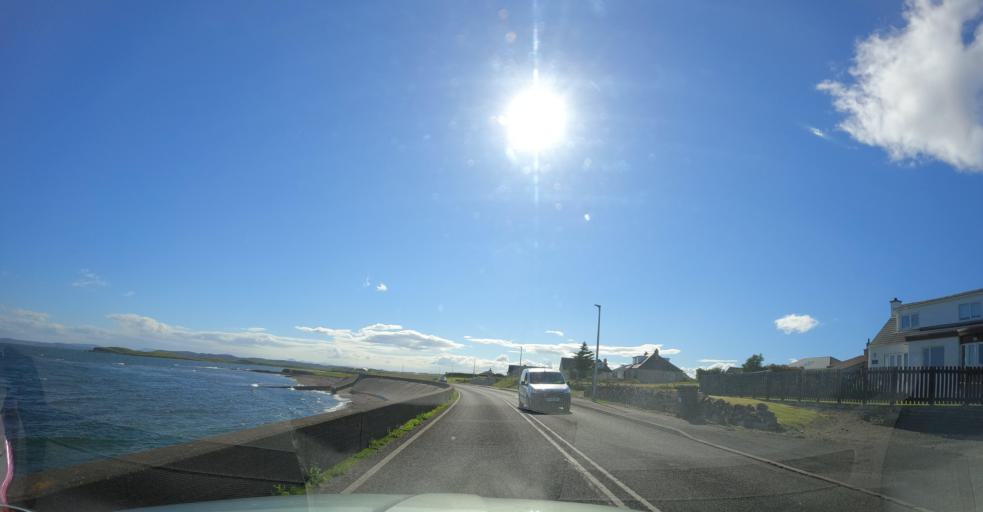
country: GB
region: Scotland
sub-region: Eilean Siar
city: Stornoway
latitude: 58.2054
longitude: -6.3087
